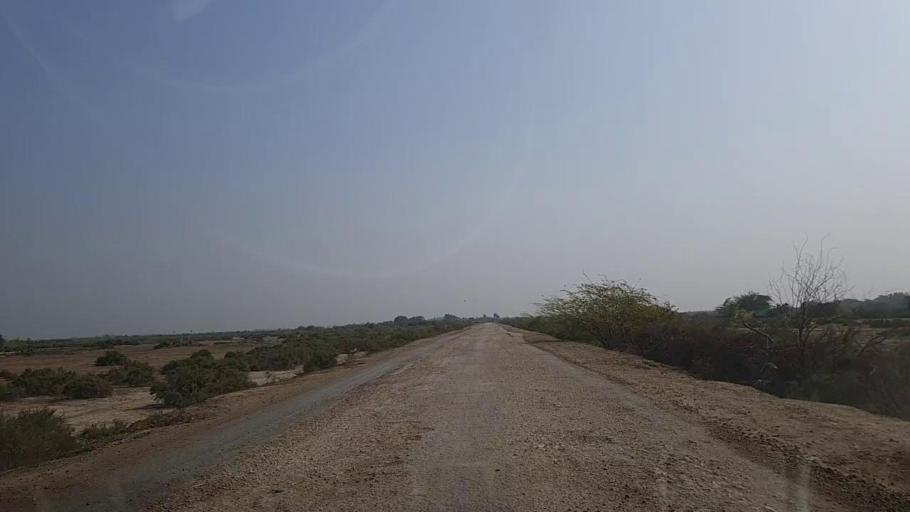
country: PK
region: Sindh
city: Keti Bandar
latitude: 24.2533
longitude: 67.6257
